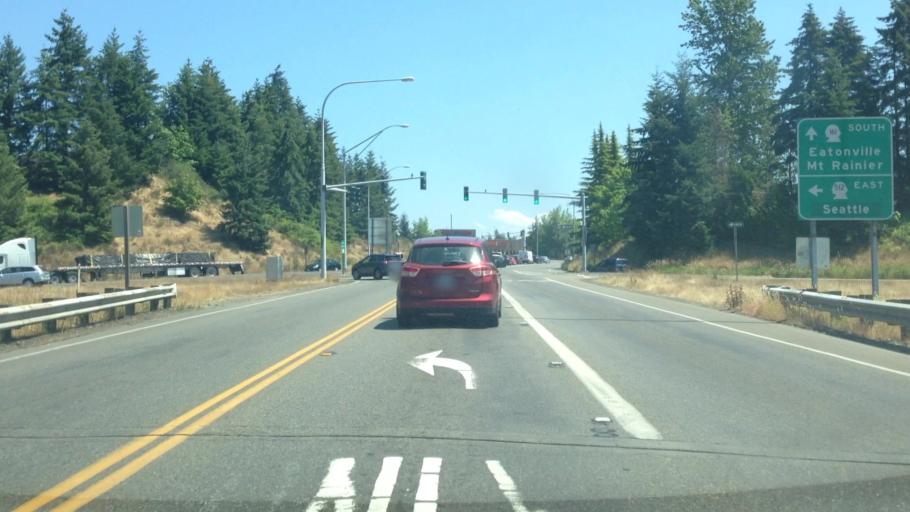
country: US
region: Washington
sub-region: Pierce County
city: Puyallup
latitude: 47.1612
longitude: -122.2969
